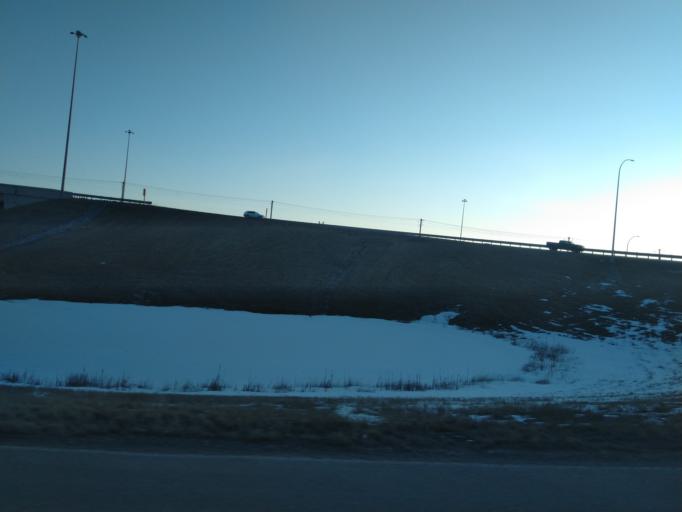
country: CA
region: Alberta
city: Calgary
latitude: 51.1294
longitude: -114.2275
